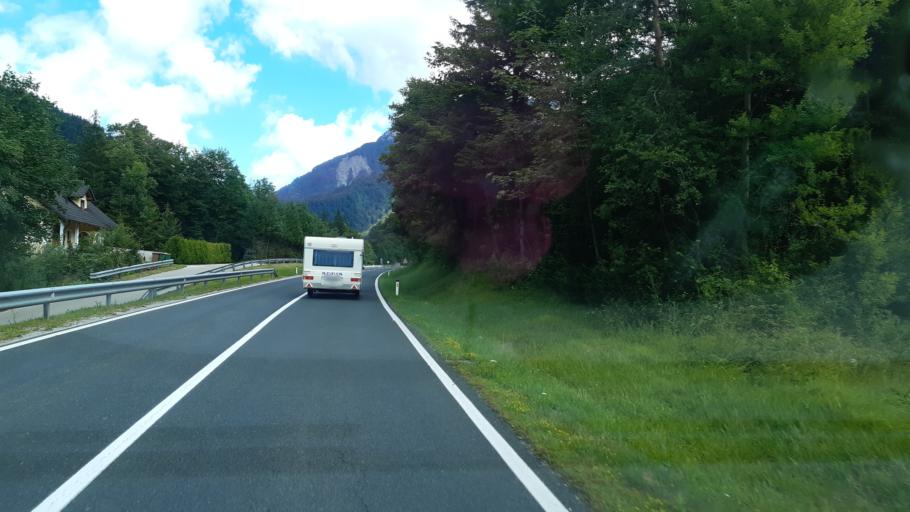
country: SI
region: Trzic
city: Trzic
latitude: 46.3868
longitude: 14.2911
